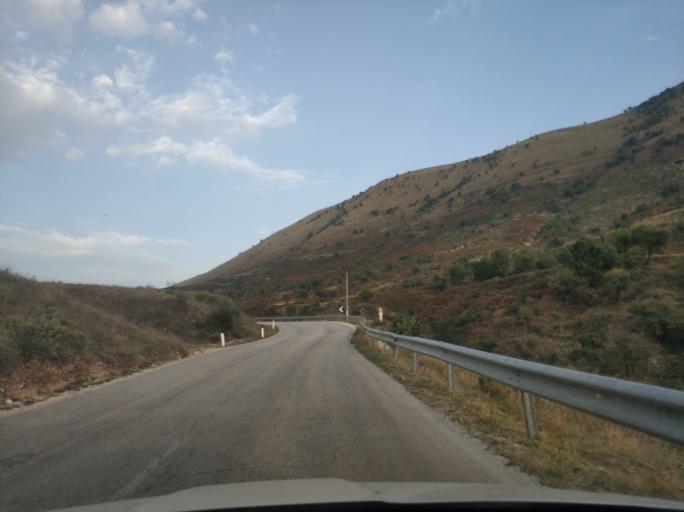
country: AL
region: Gjirokaster
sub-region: Rrethi i Gjirokastres
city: Dervician
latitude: 39.9375
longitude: 20.2167
